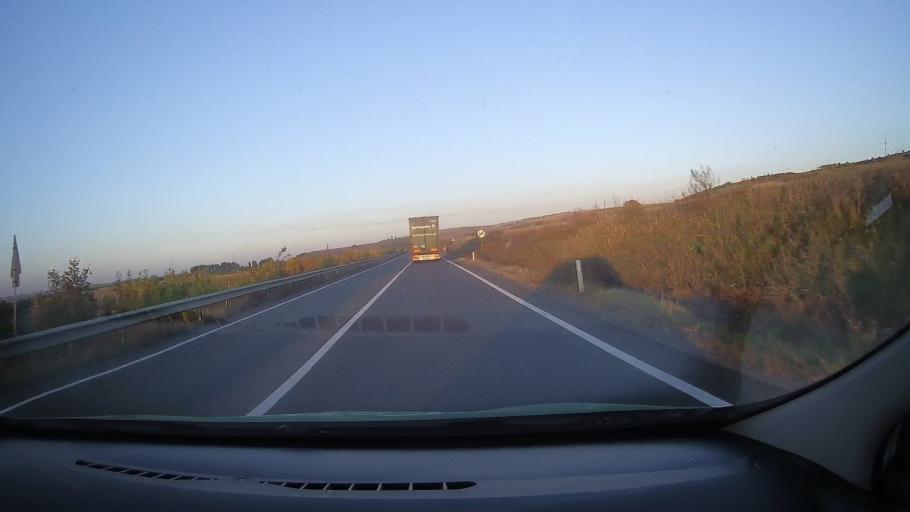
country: RO
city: Dioszeg
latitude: 47.3068
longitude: 22.0268
